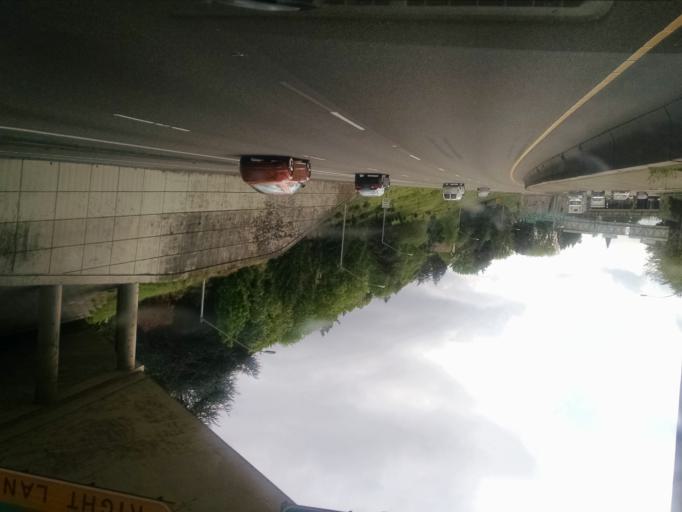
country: US
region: Oregon
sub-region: Multnomah County
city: Portland
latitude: 45.5117
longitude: -122.6890
